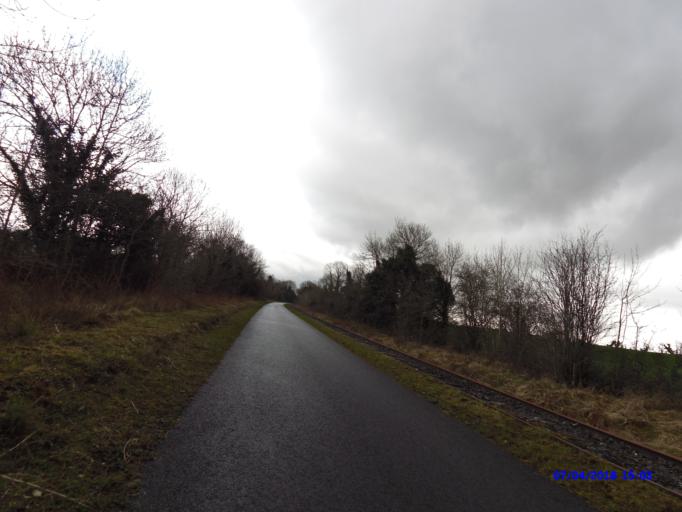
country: IE
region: Leinster
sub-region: An Iarmhi
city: Athlone
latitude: 53.4112
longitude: -7.8392
